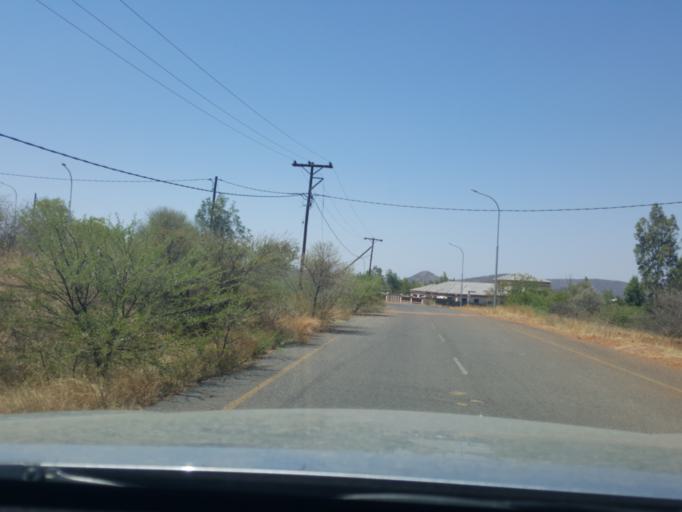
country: BW
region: South East
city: Lobatse
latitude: -25.1883
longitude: 25.6773
